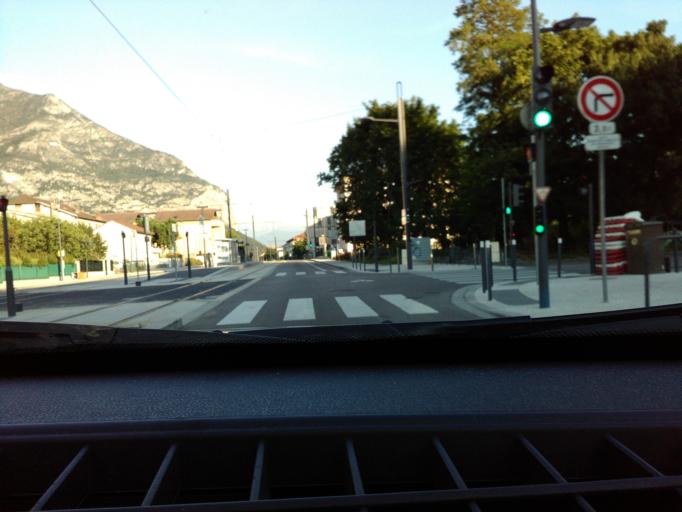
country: FR
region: Rhone-Alpes
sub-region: Departement de l'Isere
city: Saint-Egreve
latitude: 45.2358
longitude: 5.6754
